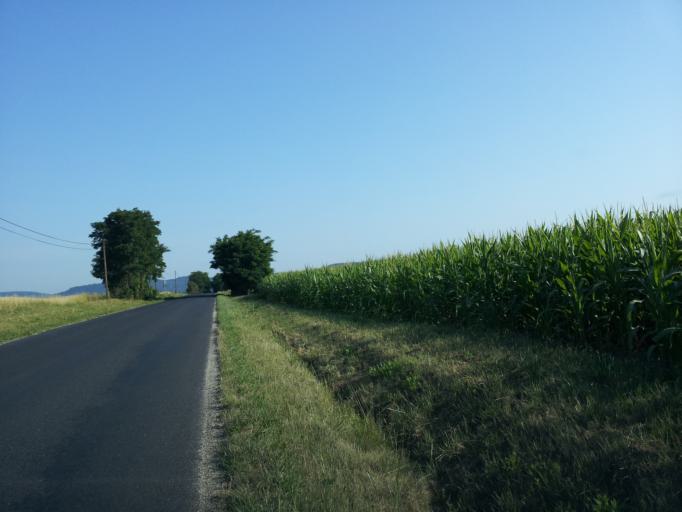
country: HU
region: Zala
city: Gyenesdias
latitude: 46.8568
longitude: 17.3012
